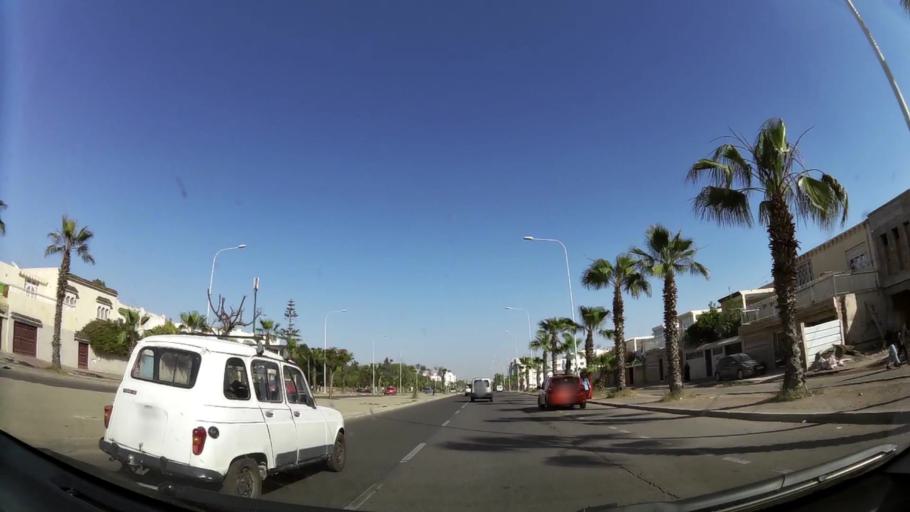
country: MA
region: Oued ed Dahab-Lagouira
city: Dakhla
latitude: 30.4071
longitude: -9.5545
